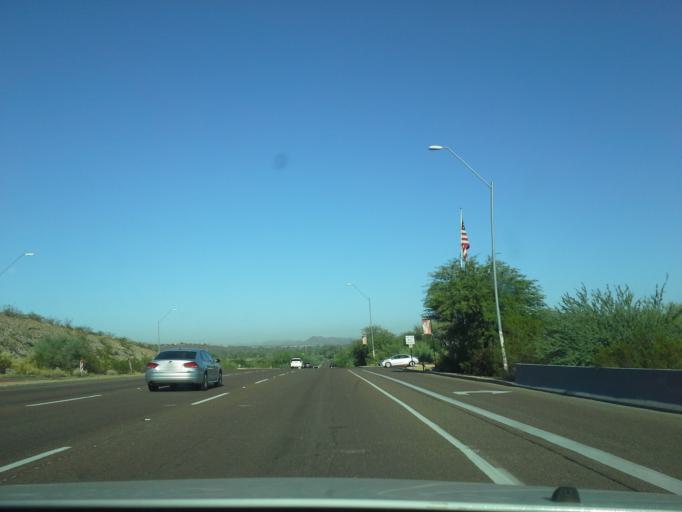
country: US
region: Arizona
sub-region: Maricopa County
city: Paradise Valley
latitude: 33.6006
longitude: -112.0479
